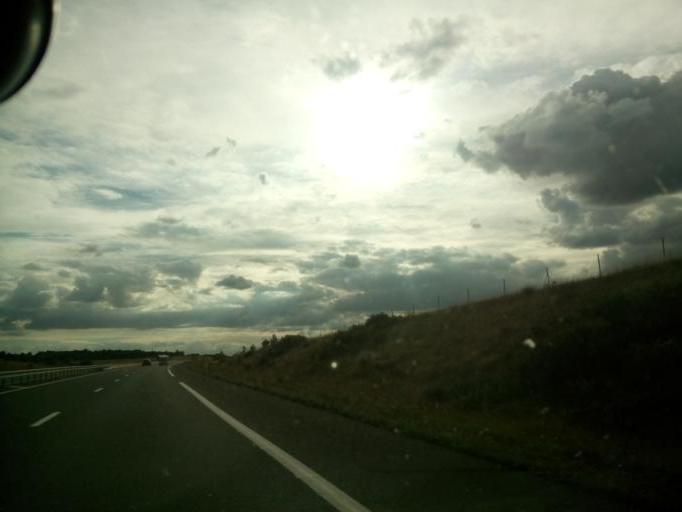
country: FR
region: Centre
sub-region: Departement du Loir-et-Cher
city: Faverolles-sur-Cher
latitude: 47.2963
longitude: 1.1904
